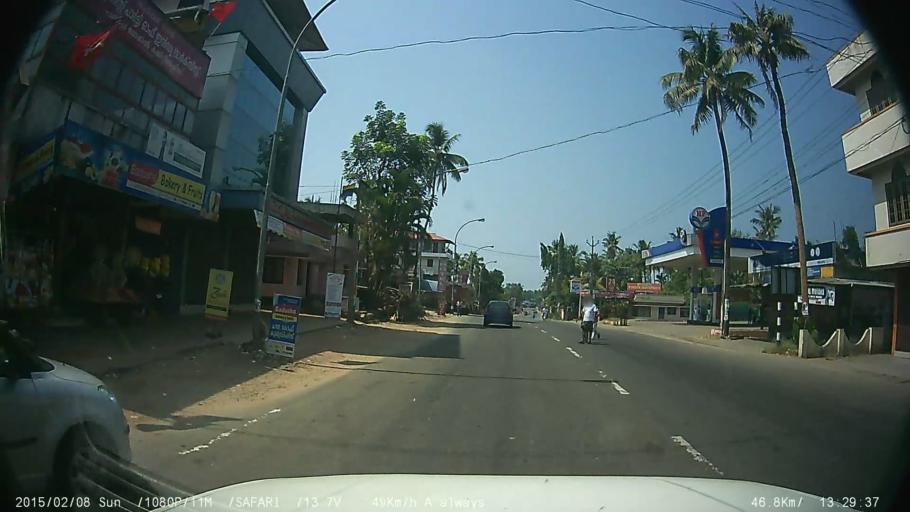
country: IN
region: Kerala
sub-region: Ernakulam
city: Muvattupula
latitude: 10.0188
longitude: 76.5632
